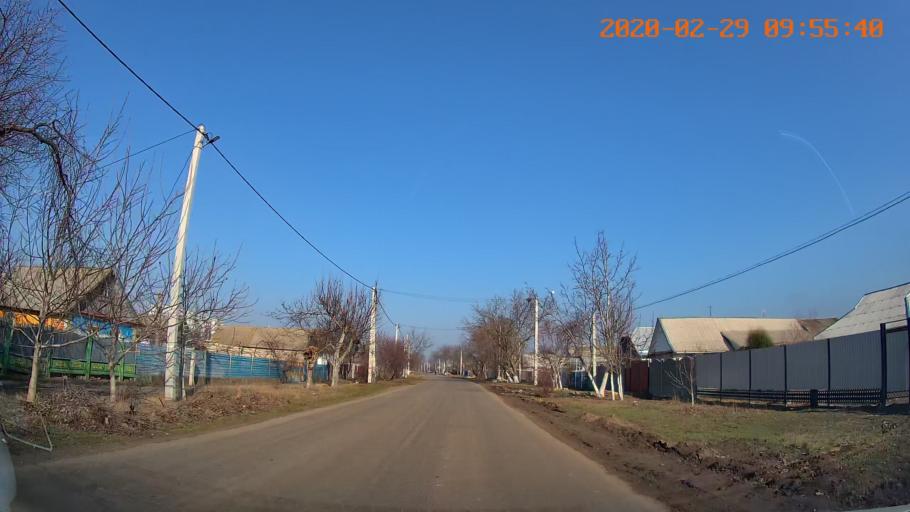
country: MD
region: Telenesti
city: Slobozia
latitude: 46.7359
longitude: 29.7089
